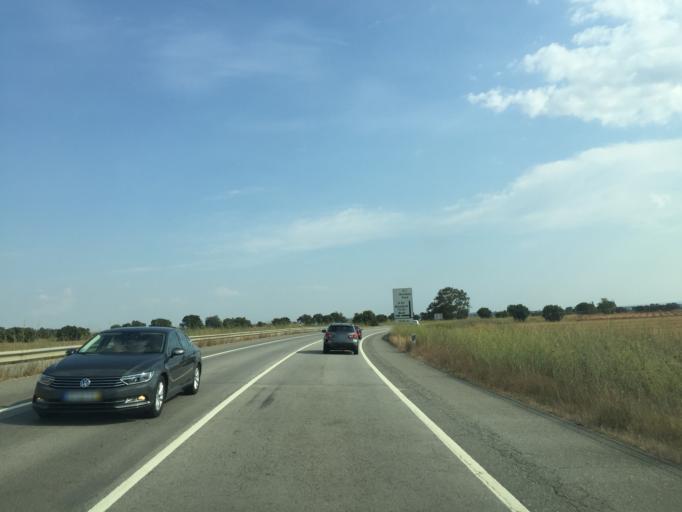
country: PT
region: Beja
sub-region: Aljustrel
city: Aljustrel
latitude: 37.9357
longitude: -8.3609
